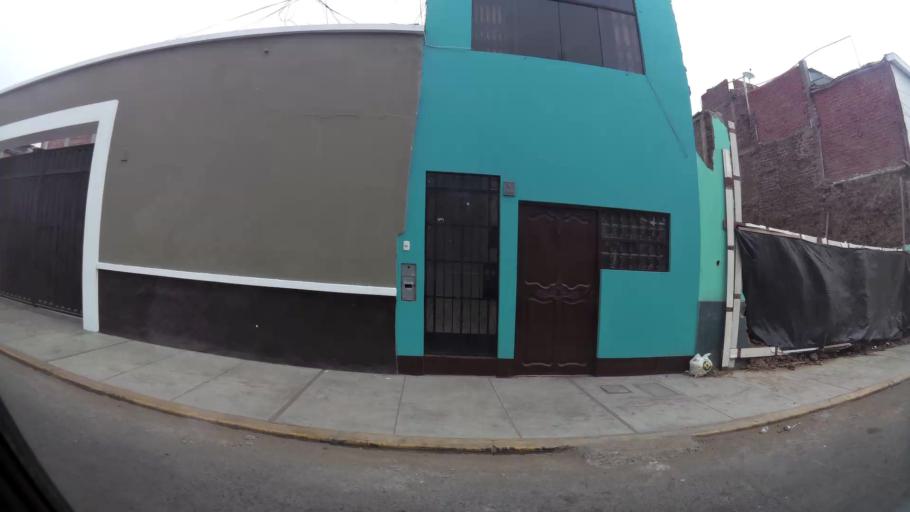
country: PE
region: La Libertad
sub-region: Provincia de Trujillo
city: Trujillo
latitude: -8.1144
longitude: -79.0305
